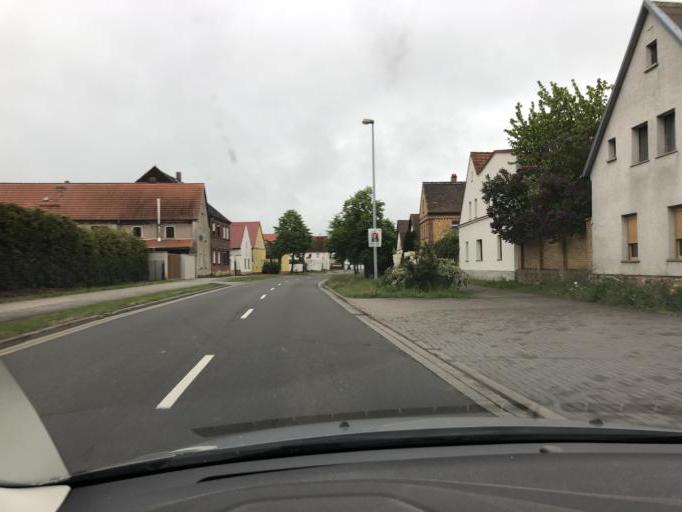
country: DE
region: Saxony
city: Krostitz
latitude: 51.4849
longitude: 12.4121
